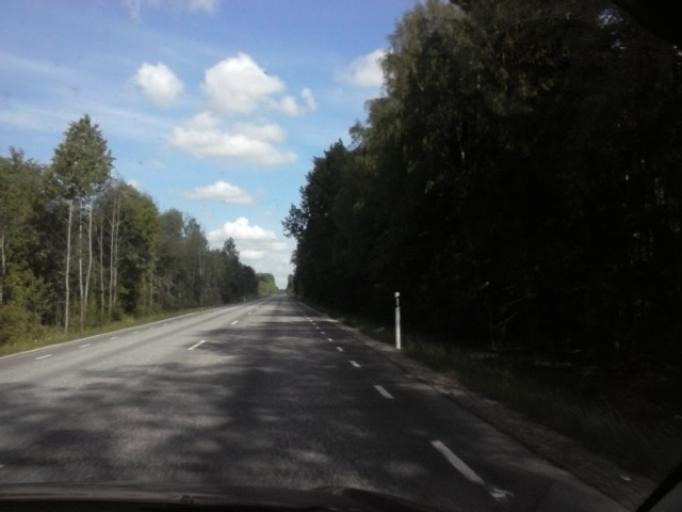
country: EE
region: Raplamaa
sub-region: Maerjamaa vald
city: Marjamaa
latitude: 58.9447
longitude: 24.5790
